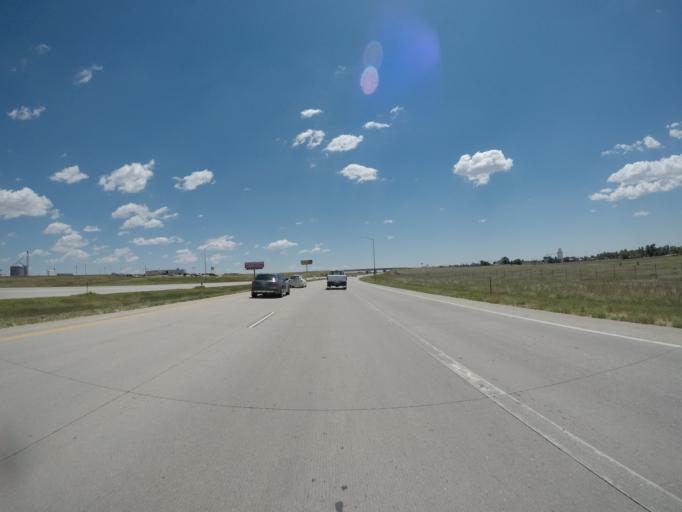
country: US
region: Colorado
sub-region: Lincoln County
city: Limon
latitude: 39.2724
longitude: -103.6820
